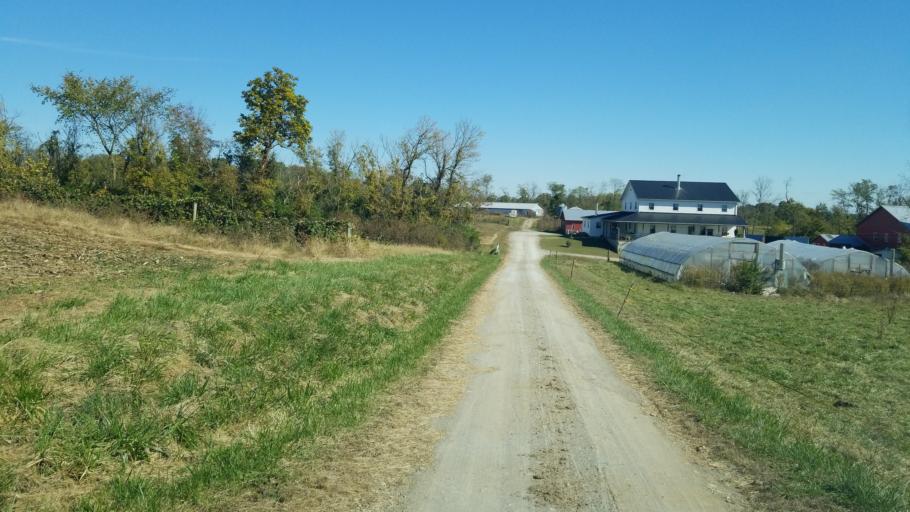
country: US
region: Ohio
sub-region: Highland County
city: Leesburg
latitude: 39.2823
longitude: -83.4763
